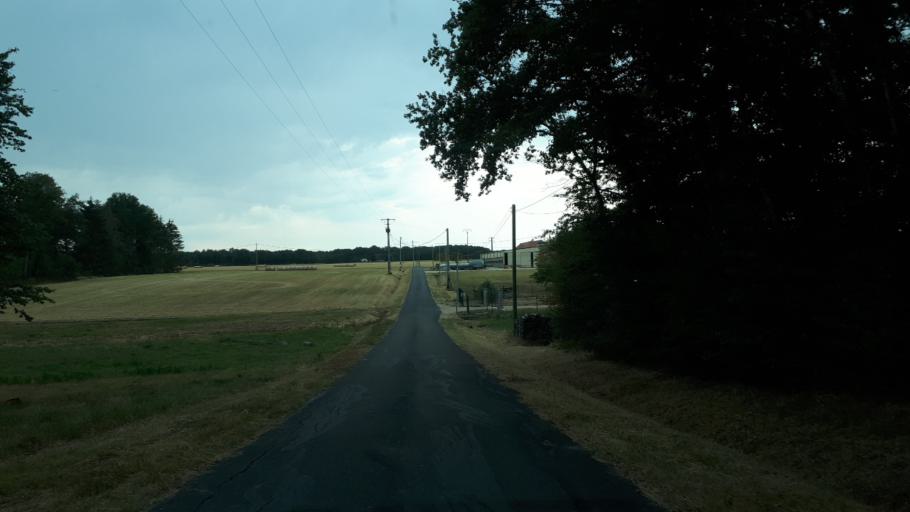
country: FR
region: Centre
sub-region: Departement du Loir-et-Cher
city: Saint-Romain-sur-Cher
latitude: 47.3563
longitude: 1.3961
